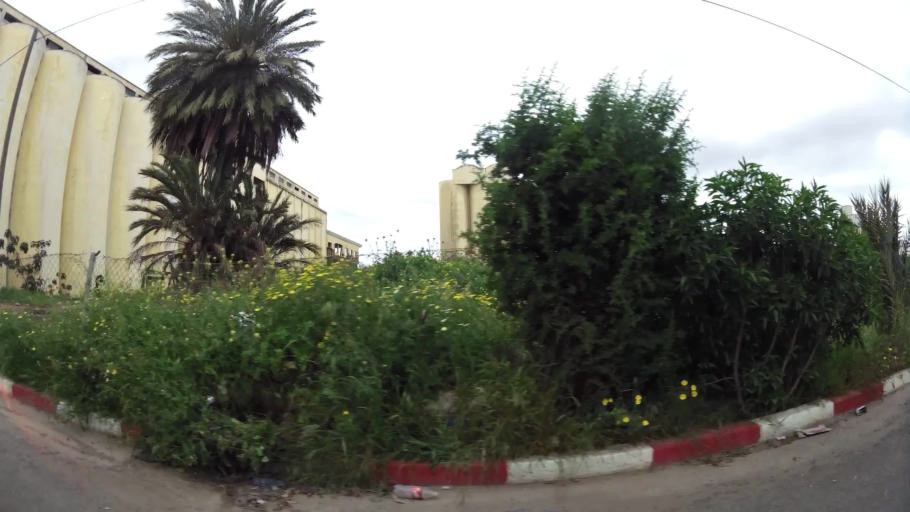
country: MA
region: Grand Casablanca
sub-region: Casablanca
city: Casablanca
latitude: 33.5483
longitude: -7.6403
